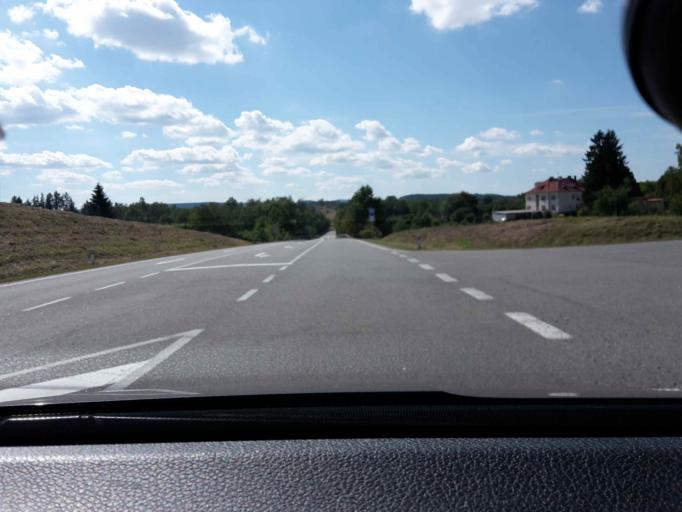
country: CZ
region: Jihocesky
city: Strmilov
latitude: 49.1622
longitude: 15.2094
